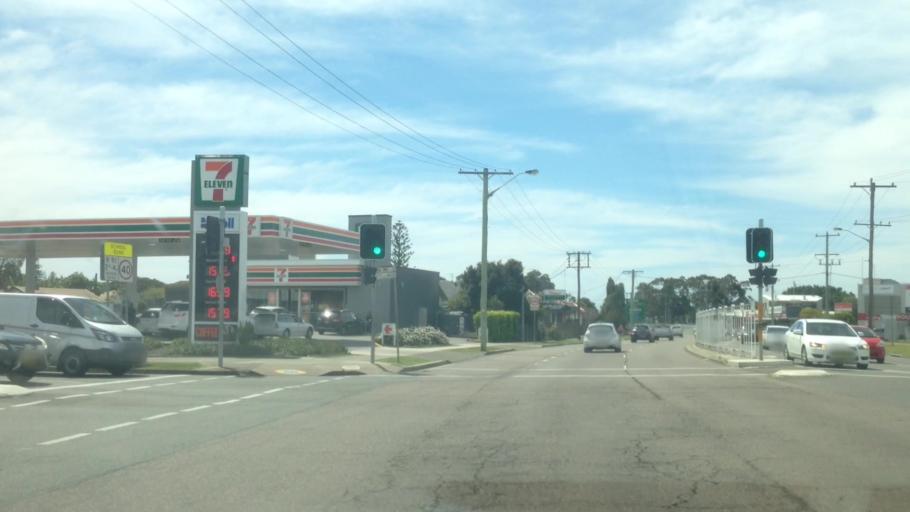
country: AU
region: New South Wales
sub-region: Newcastle
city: Broadmeadow
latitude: -32.9183
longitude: 151.7244
